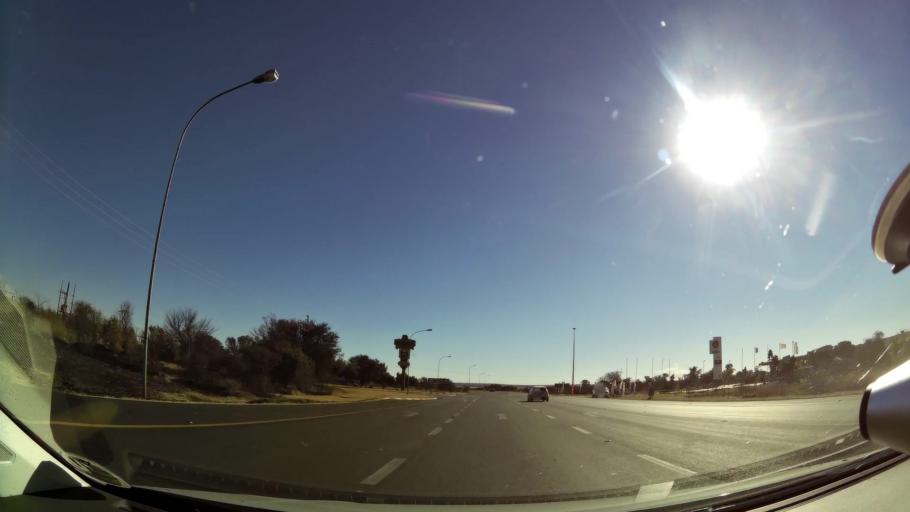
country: ZA
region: Northern Cape
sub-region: Frances Baard District Municipality
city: Kimberley
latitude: -28.6922
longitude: 24.7781
